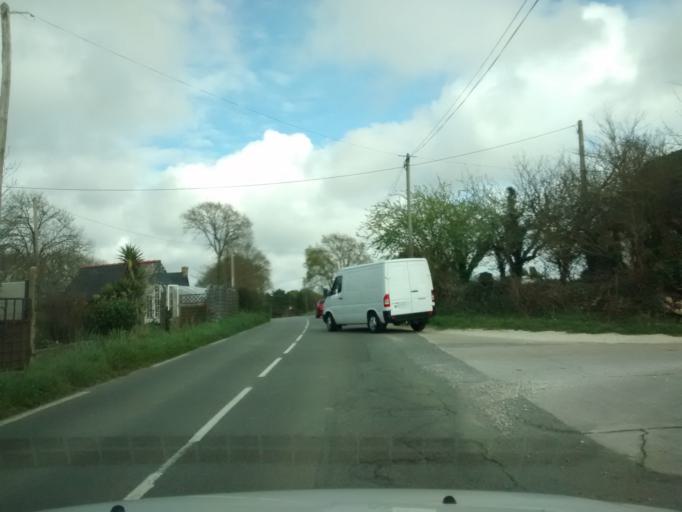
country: FR
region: Brittany
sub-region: Departement du Morbihan
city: Gestel
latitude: 47.7797
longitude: -3.4520
